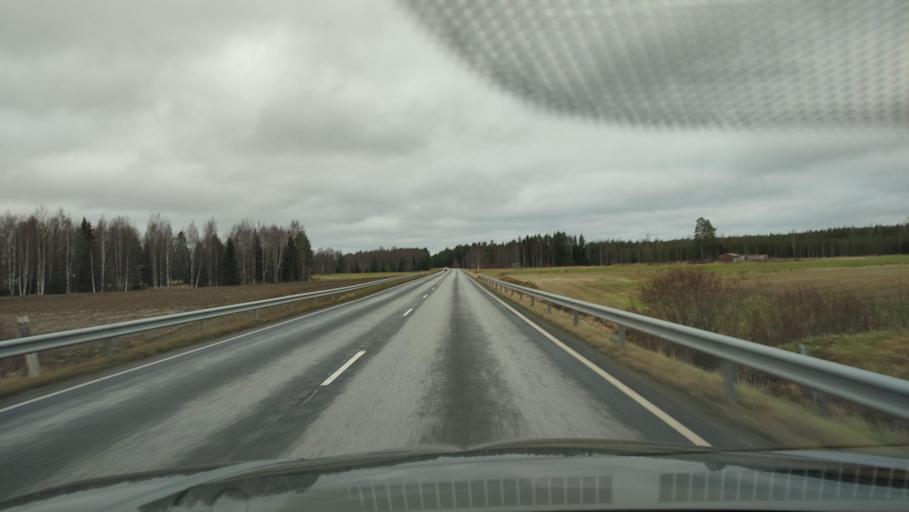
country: FI
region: Southern Ostrobothnia
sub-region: Suupohja
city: Kauhajoki
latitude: 62.4857
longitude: 22.2875
